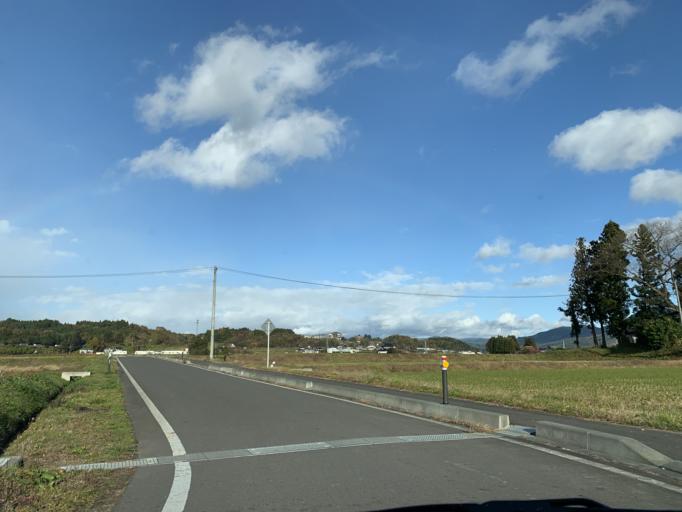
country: JP
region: Iwate
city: Ichinoseki
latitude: 39.0111
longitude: 141.0967
